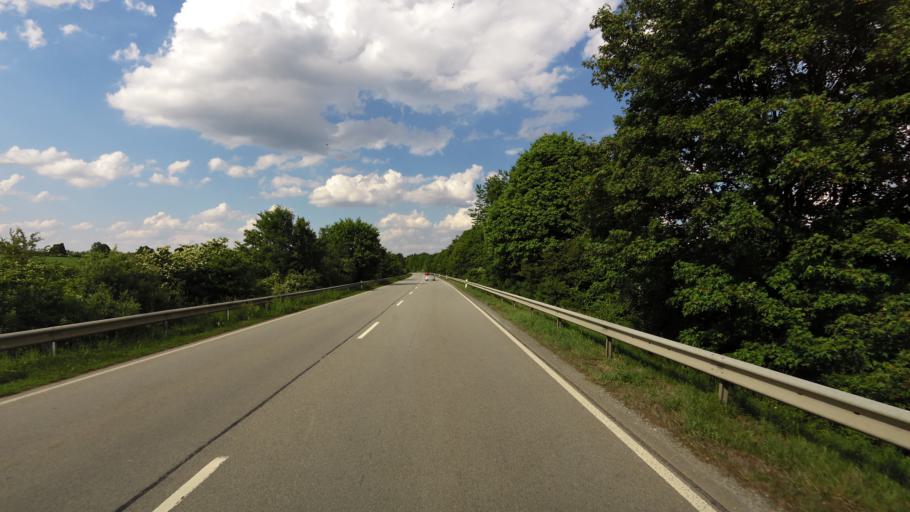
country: DE
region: Bavaria
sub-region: Upper Bavaria
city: Edling
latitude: 48.0546
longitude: 12.1932
